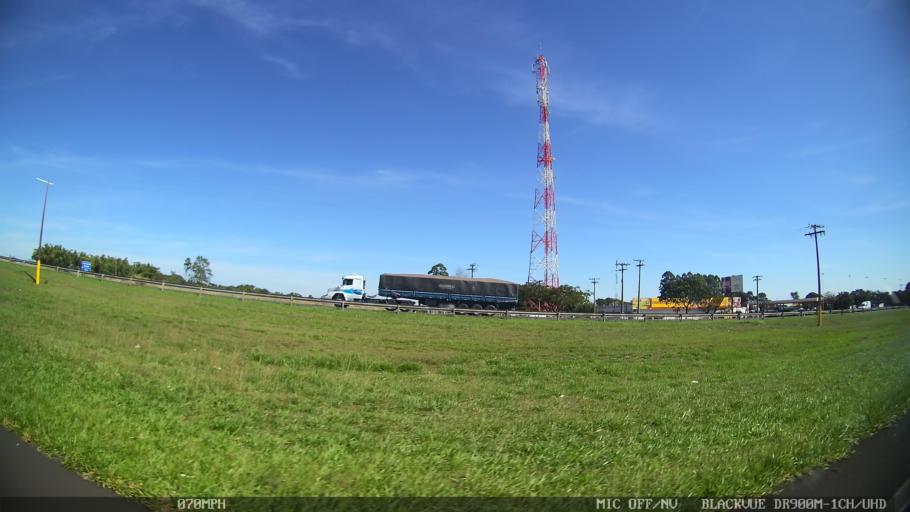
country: BR
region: Sao Paulo
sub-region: Santa Rita Do Passa Quatro
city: Santa Rita do Passa Quatro
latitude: -21.6797
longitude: -47.6035
